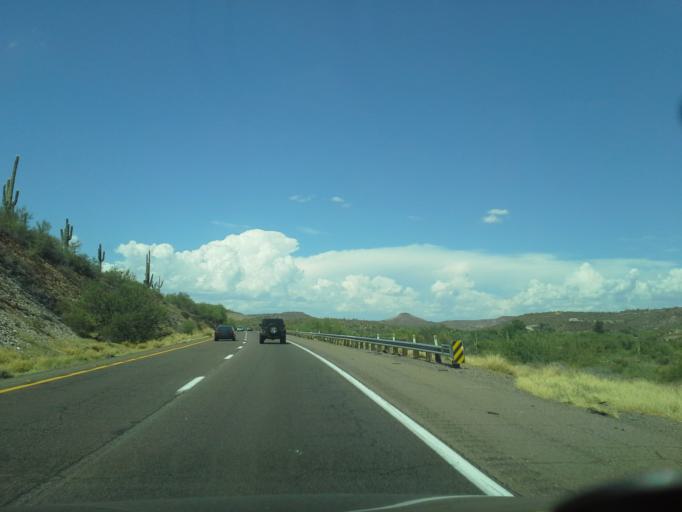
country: US
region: Arizona
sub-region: Maricopa County
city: New River
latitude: 33.9340
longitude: -112.1400
